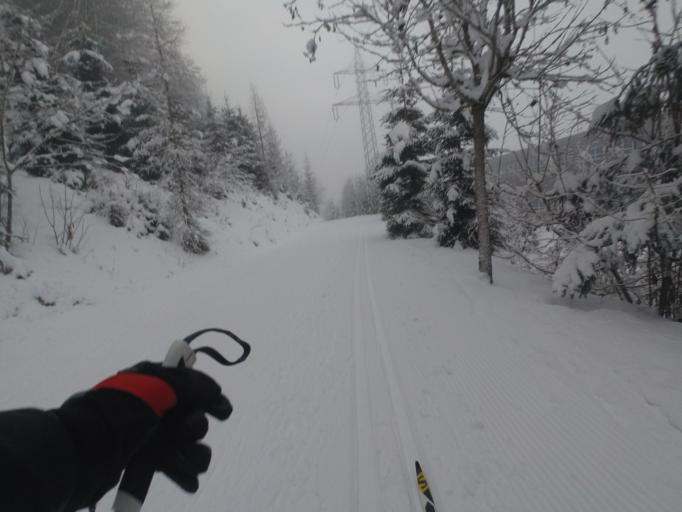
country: AT
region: Salzburg
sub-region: Politischer Bezirk Sankt Johann im Pongau
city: Wagrain
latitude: 47.3521
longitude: 13.3239
